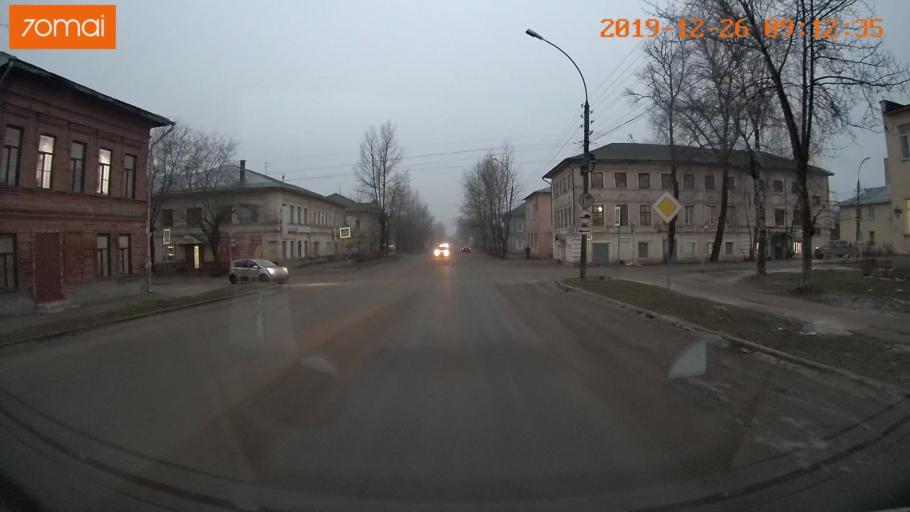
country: RU
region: Vologda
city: Gryazovets
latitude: 58.8819
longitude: 40.2535
